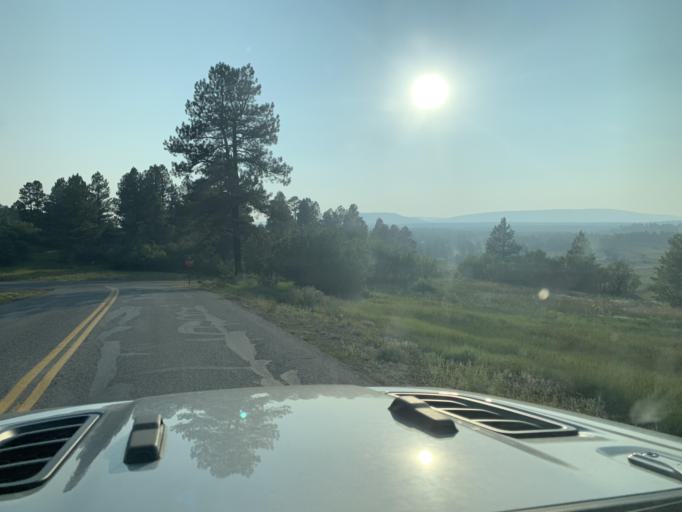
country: US
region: Colorado
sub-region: Archuleta County
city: Pagosa Springs
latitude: 37.2895
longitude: -107.0975
